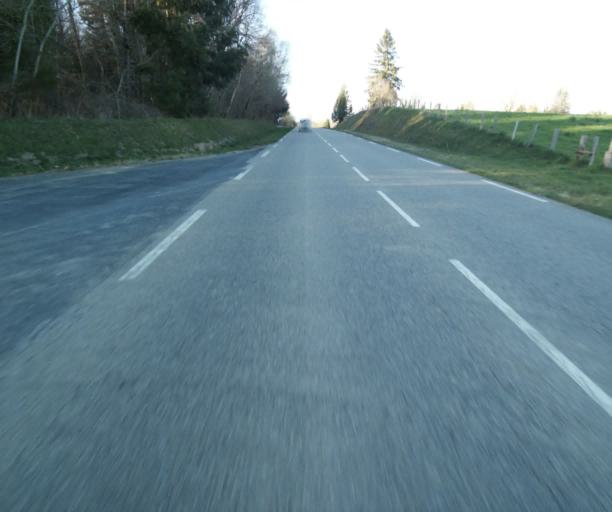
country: FR
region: Limousin
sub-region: Departement de la Correze
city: Seilhac
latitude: 45.3824
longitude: 1.7216
